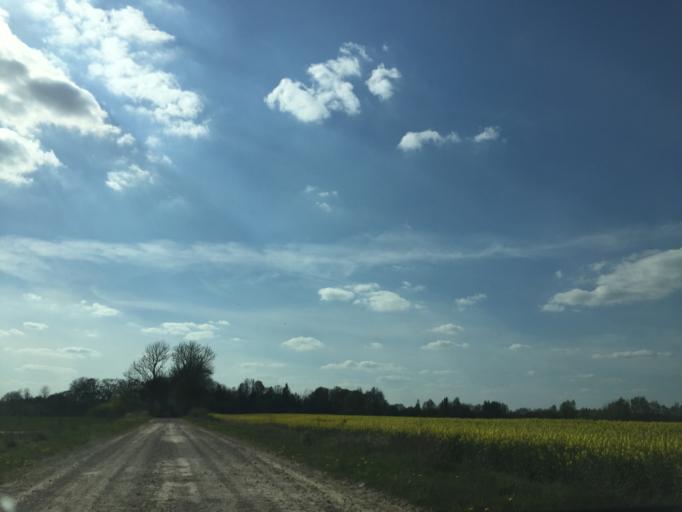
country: LV
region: Lecava
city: Iecava
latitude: 56.5104
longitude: 24.3292
